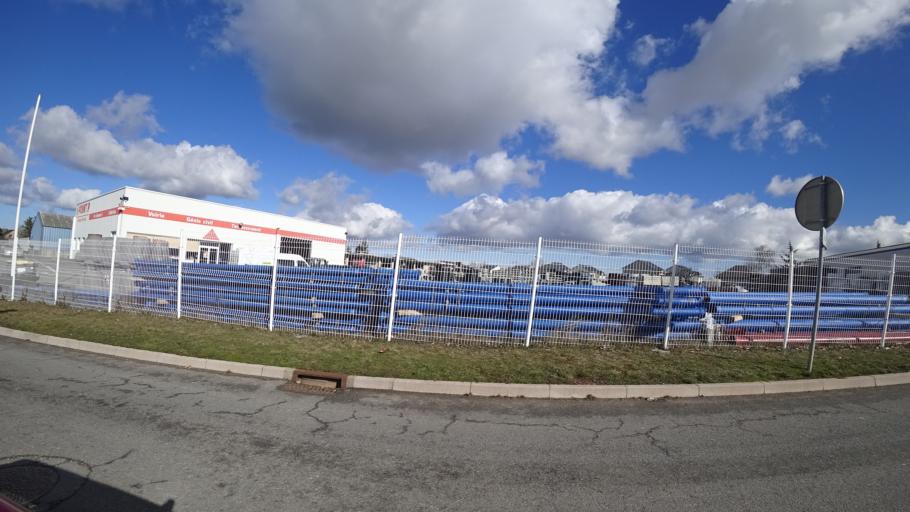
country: FR
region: Midi-Pyrenees
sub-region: Departement de l'Aveyron
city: Olemps
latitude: 44.3739
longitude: 2.5504
